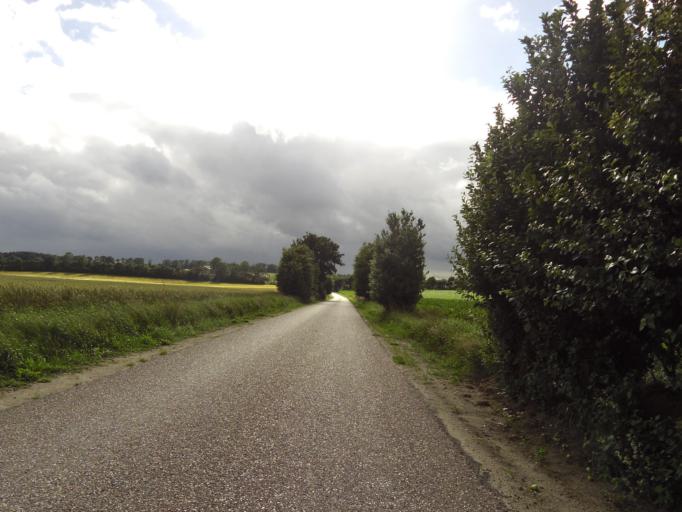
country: DK
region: South Denmark
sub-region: Tonder Kommune
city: Toftlund
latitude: 55.1313
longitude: 9.1090
